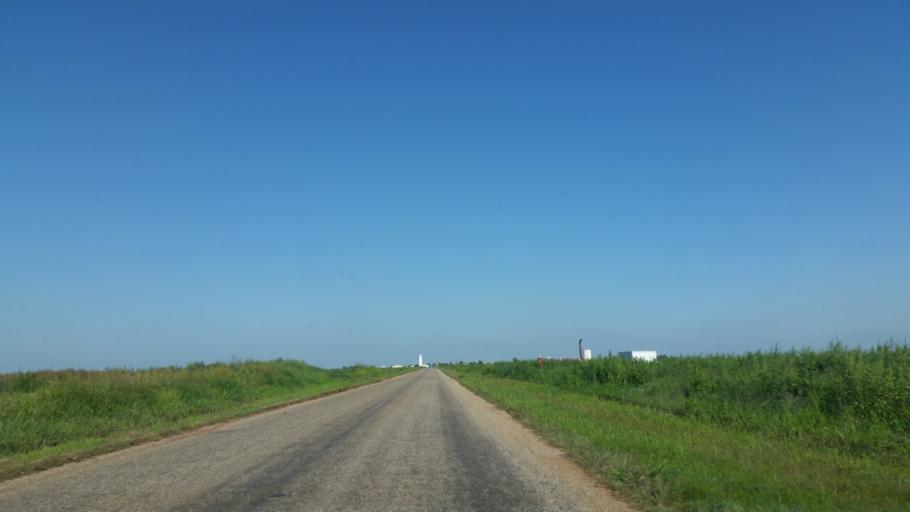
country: US
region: New Mexico
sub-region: Curry County
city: Clovis
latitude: 34.4630
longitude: -103.2235
